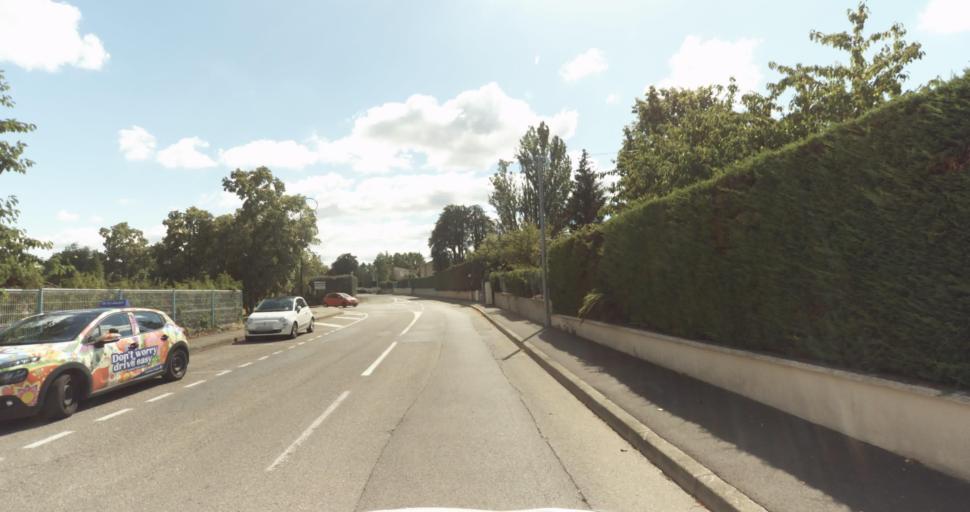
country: FR
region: Rhone-Alpes
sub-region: Departement du Rhone
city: Chaponost
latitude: 45.7075
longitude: 4.7407
